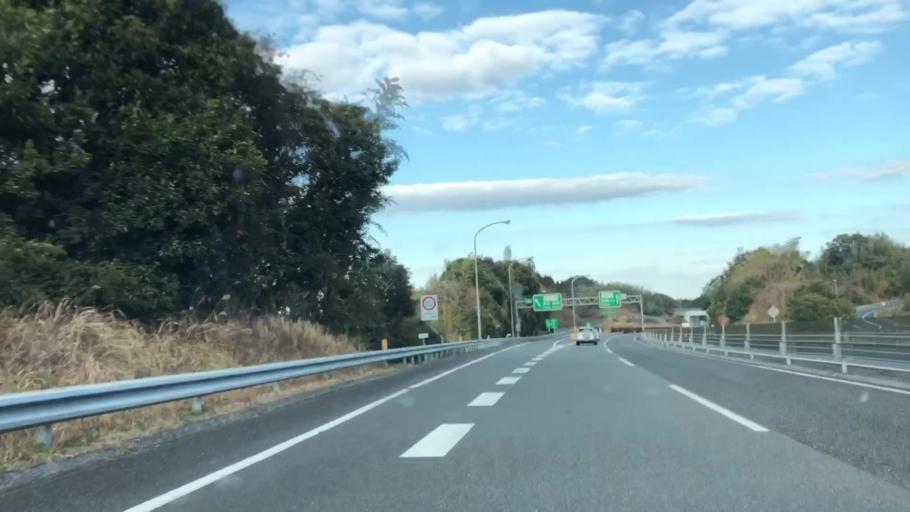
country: JP
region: Miyazaki
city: Miyazaki-shi
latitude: 31.8457
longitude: 131.3533
